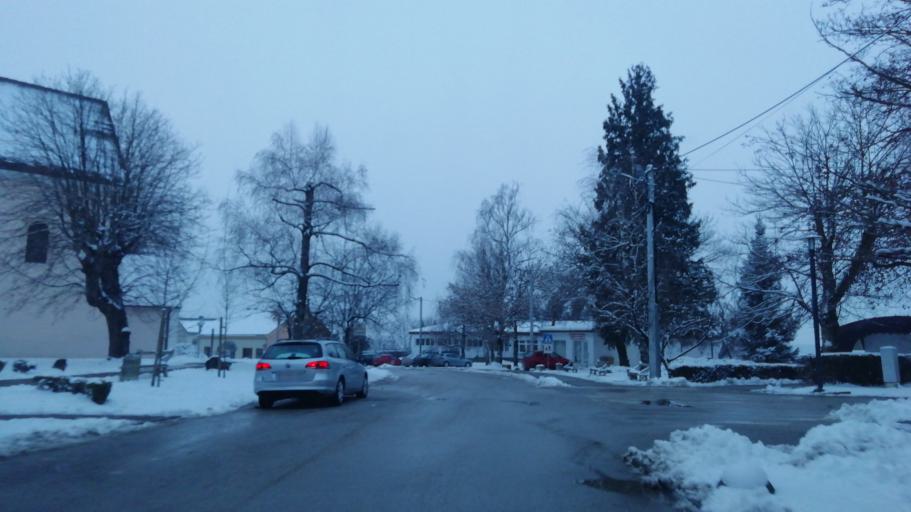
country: HR
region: Zagrebacka
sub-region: Grad Vrbovec
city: Vrbovec
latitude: 45.8849
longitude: 16.4176
